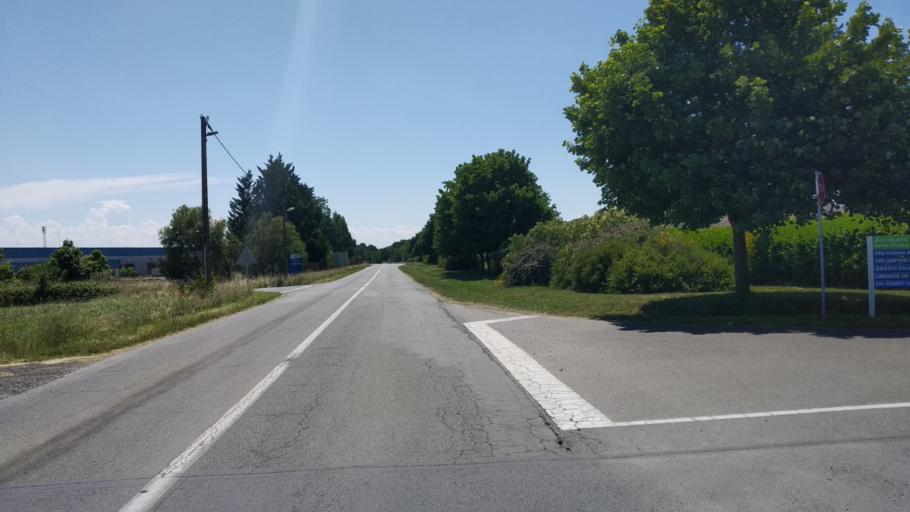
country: FR
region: Poitou-Charentes
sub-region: Departement de la Vienne
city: Migne-Auxances
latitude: 46.6039
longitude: 0.3073
